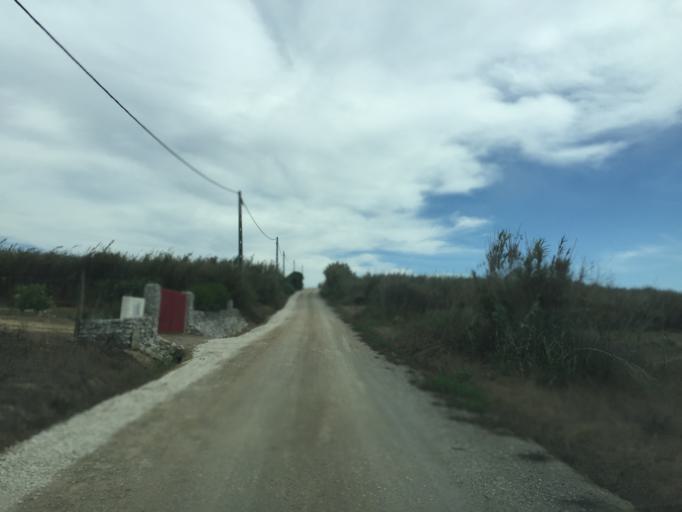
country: PT
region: Lisbon
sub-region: Lourinha
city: Lourinha
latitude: 39.1977
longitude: -9.3447
